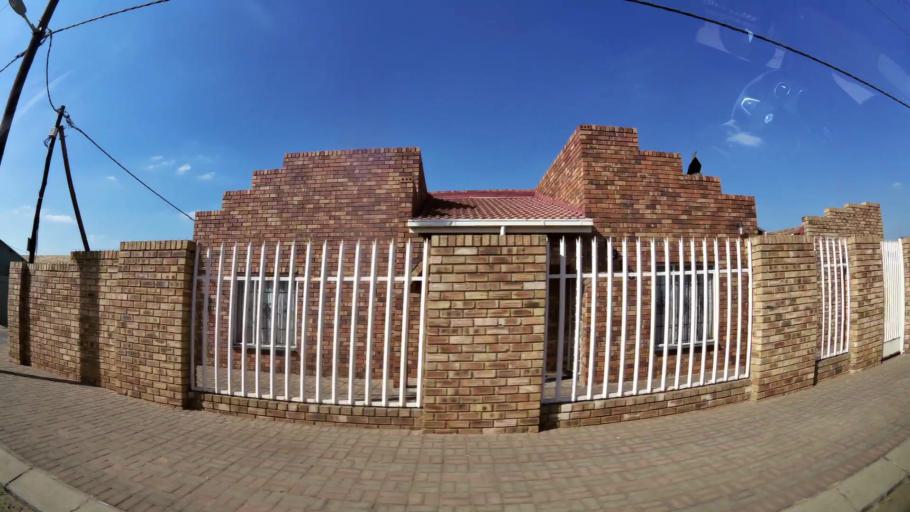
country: ZA
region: Gauteng
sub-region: City of Johannesburg Metropolitan Municipality
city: Roodepoort
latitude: -26.1626
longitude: 27.7979
